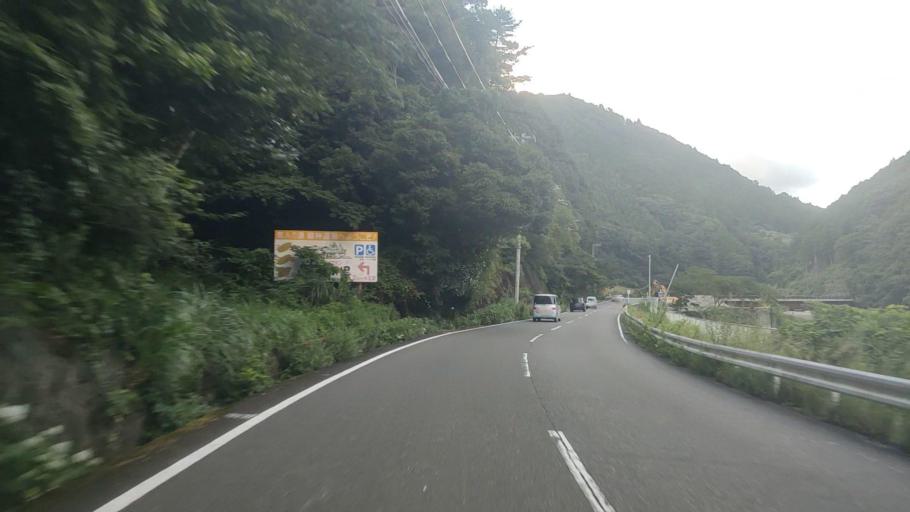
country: JP
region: Wakayama
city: Tanabe
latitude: 33.7702
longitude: 135.4998
